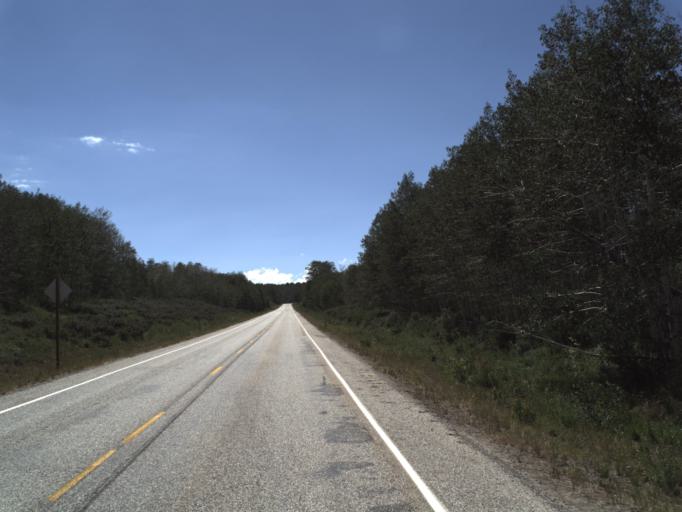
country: US
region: Utah
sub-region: Rich County
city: Randolph
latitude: 41.4760
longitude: -111.4355
